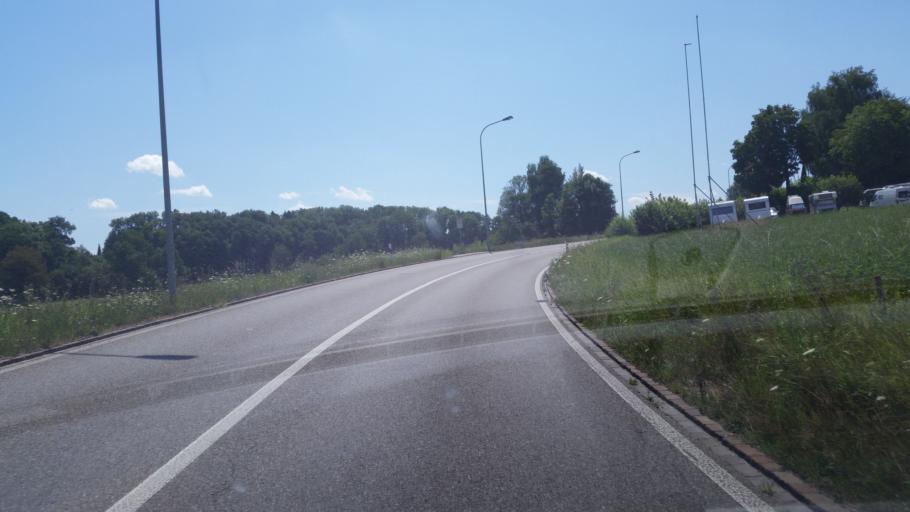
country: CH
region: Zurich
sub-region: Bezirk Dielsdorf
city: Niederglatt / Niederglatt (Dorfkern)
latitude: 47.4884
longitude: 8.5055
